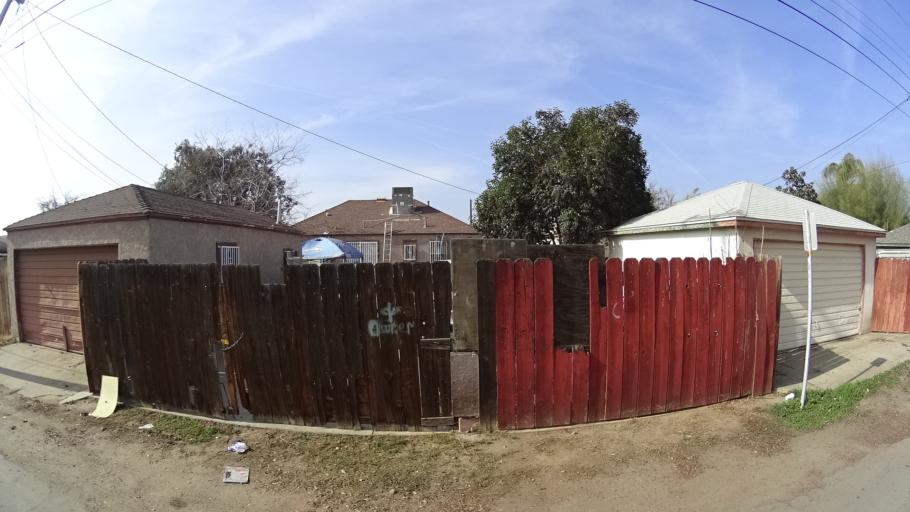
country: US
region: California
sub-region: Kern County
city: Bakersfield
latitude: 35.3404
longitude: -119.0157
